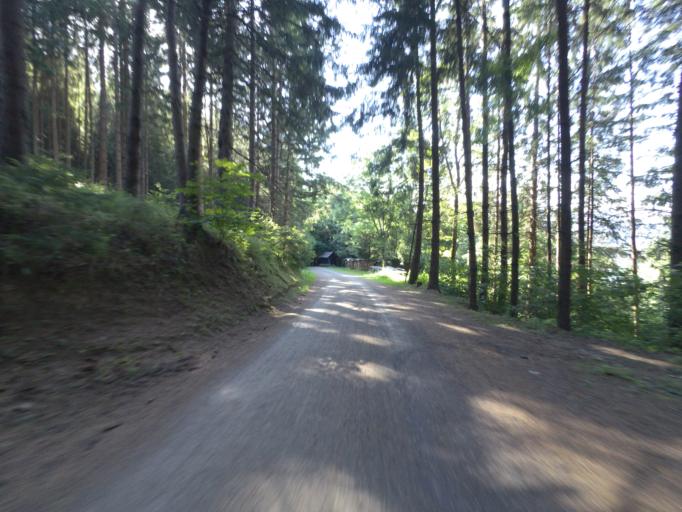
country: AT
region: Carinthia
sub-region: Politischer Bezirk Spittal an der Drau
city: Seeboden
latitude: 46.8086
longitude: 13.5226
